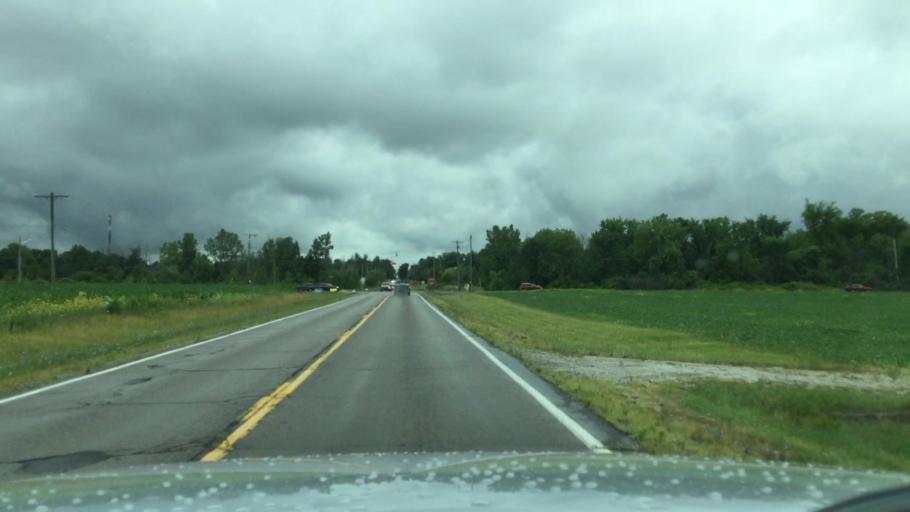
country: US
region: Michigan
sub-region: Genesee County
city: Clio
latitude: 43.1204
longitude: -83.7738
